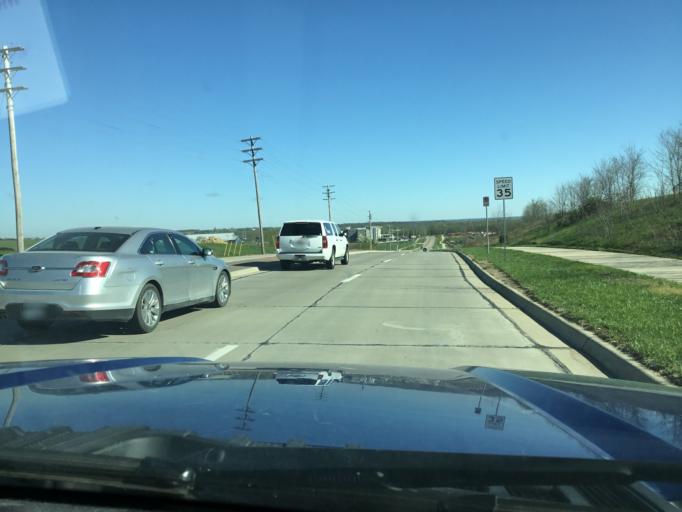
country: US
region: Kansas
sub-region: Douglas County
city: Lawrence
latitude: 38.9720
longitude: -95.3256
